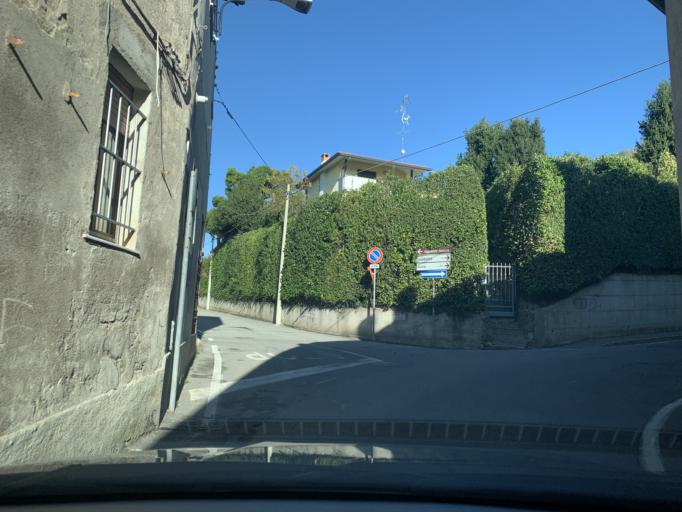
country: IT
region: Lombardy
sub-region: Provincia di Como
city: San Michele-San Giorgio
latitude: 45.6970
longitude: 9.0538
